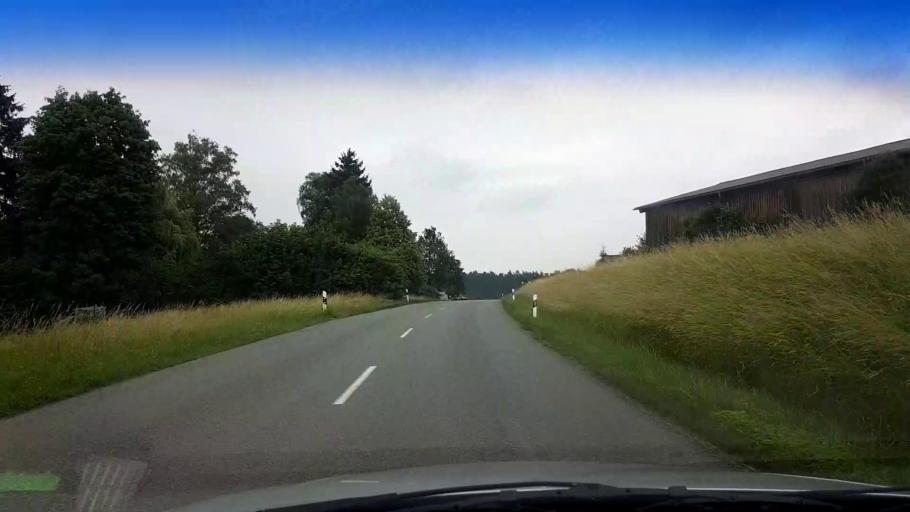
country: DE
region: Bavaria
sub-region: Upper Franconia
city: Kasendorf
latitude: 50.0770
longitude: 11.3230
